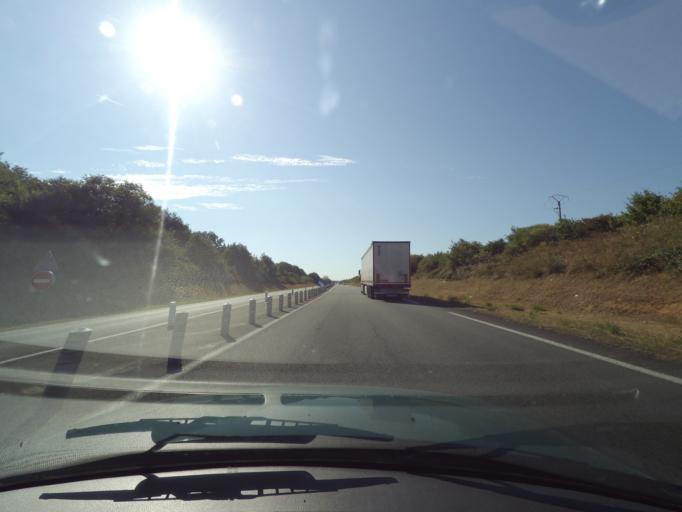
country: FR
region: Poitou-Charentes
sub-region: Departement de la Vienne
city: Savigny-Levescault
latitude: 46.5032
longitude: 0.4795
